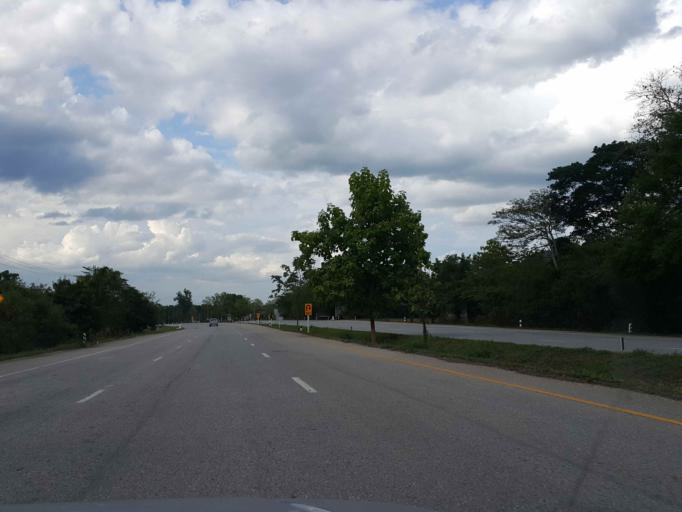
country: TH
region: Lampang
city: Thoen
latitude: 17.7317
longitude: 99.2319
